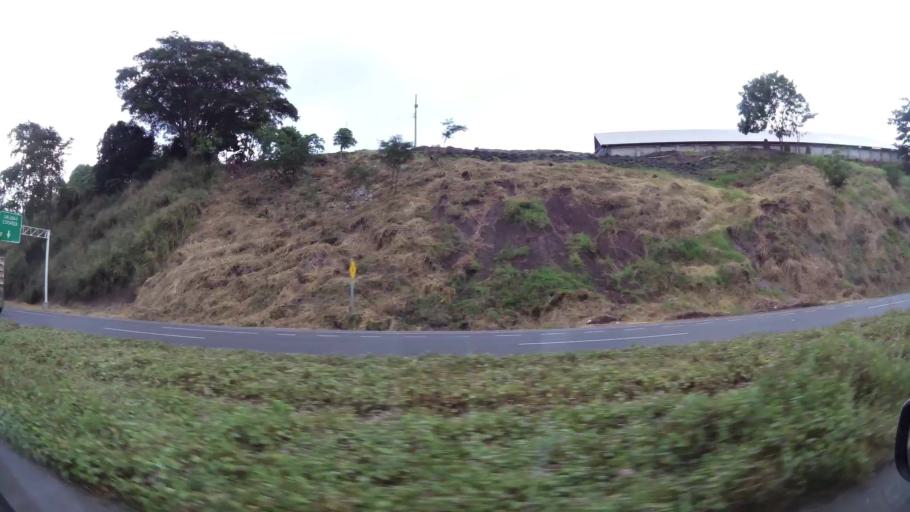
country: CR
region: Puntarenas
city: Esparza
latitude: 9.9196
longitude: -84.6968
